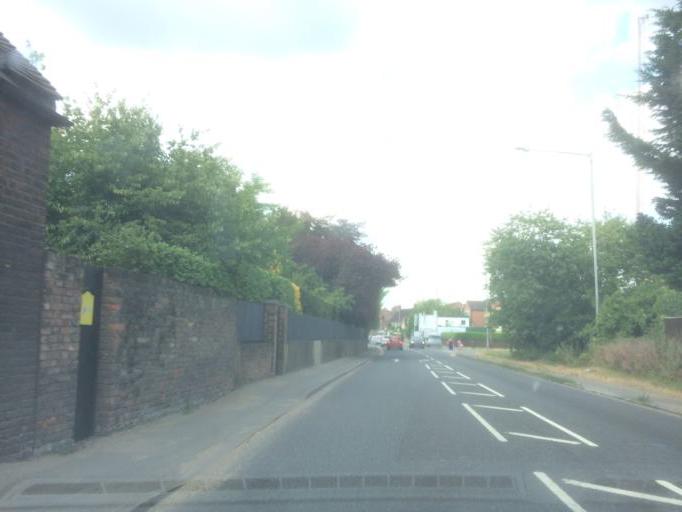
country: GB
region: England
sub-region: Buckinghamshire
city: Farnham Royal
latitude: 51.5524
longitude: -0.6156
